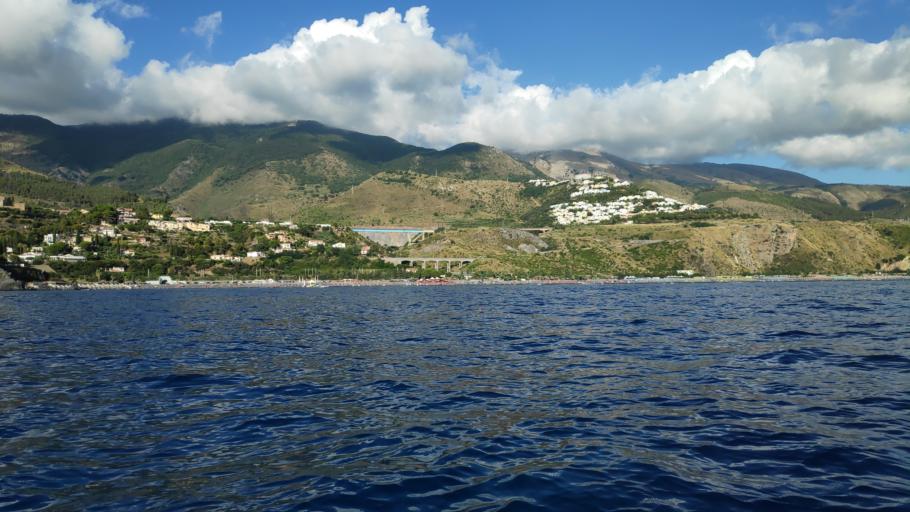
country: IT
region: Calabria
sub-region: Provincia di Cosenza
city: Praia a Mare
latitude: 39.8691
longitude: 15.7818
